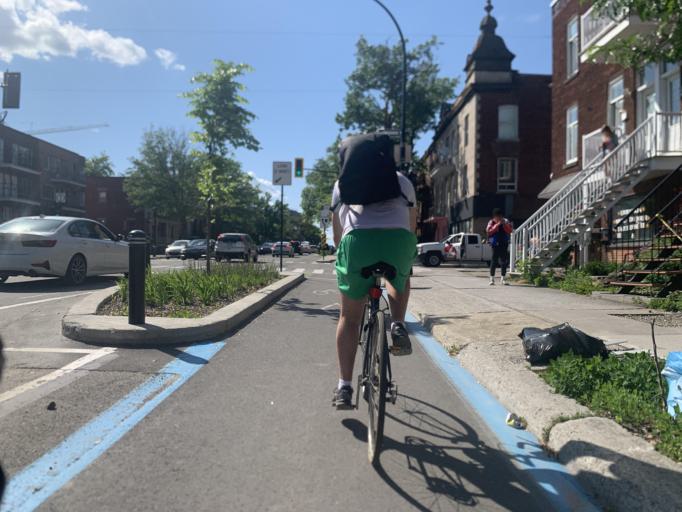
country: CA
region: Quebec
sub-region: Montreal
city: Montreal
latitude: 45.5279
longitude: -73.5913
